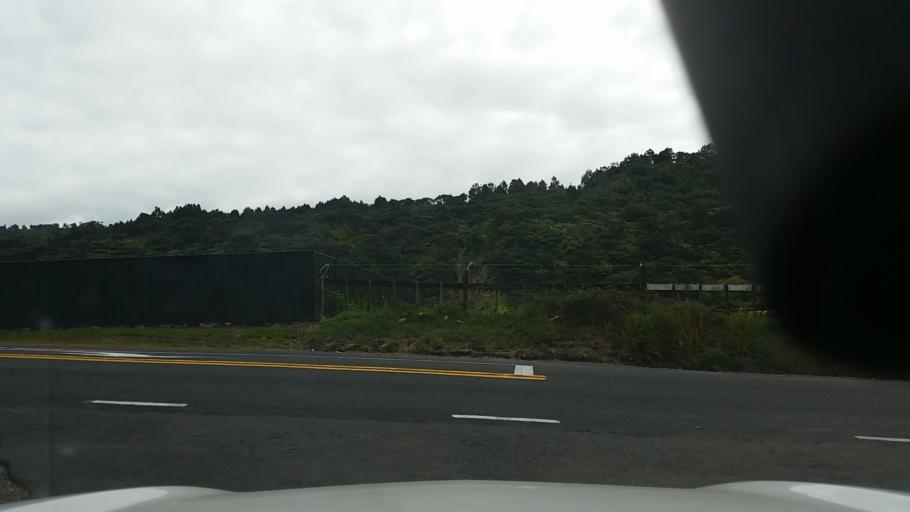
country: NZ
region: Auckland
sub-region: Auckland
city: Muriwai Beach
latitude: -36.8684
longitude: 174.5007
